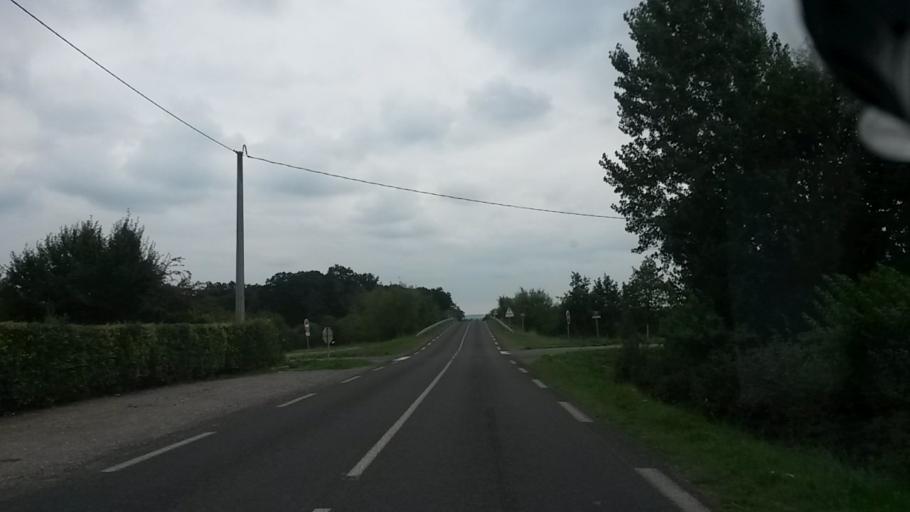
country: FR
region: Haute-Normandie
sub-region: Departement de la Seine-Maritime
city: Forges-les-Eaux
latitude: 49.6032
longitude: 1.5469
